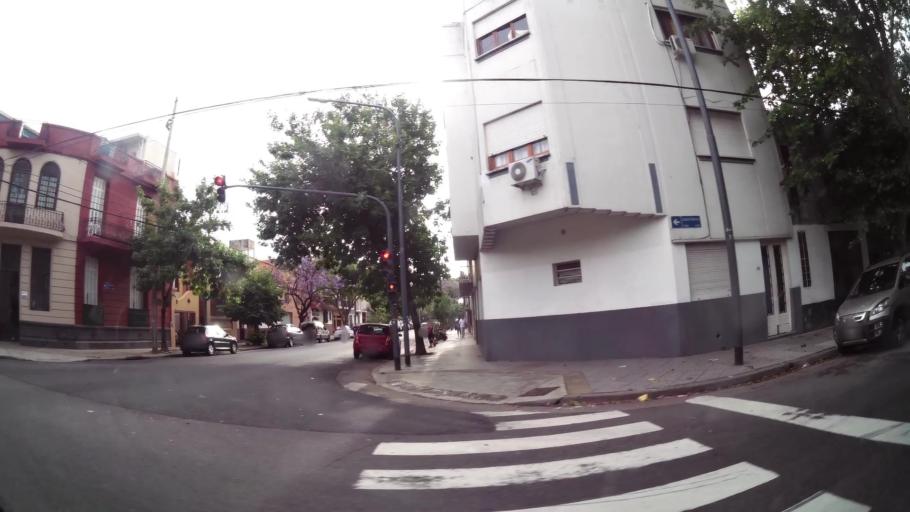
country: AR
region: Buenos Aires F.D.
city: Buenos Aires
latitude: -34.6271
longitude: -58.4185
